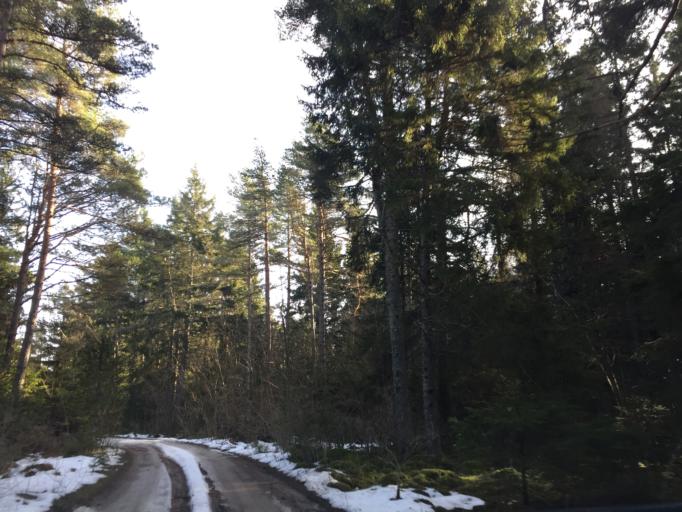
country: EE
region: Saare
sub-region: Kuressaare linn
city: Kuressaare
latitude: 58.3758
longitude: 22.0134
